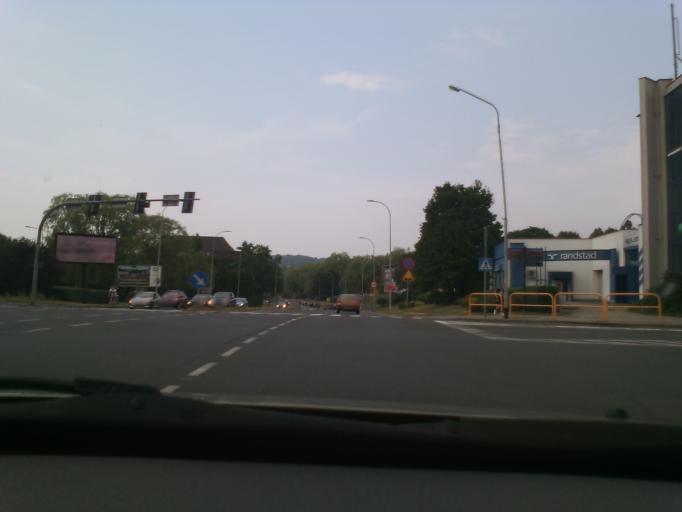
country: PL
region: Lower Silesian Voivodeship
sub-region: Powiat walbrzyski
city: Walbrzych
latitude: 50.7709
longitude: 16.2741
